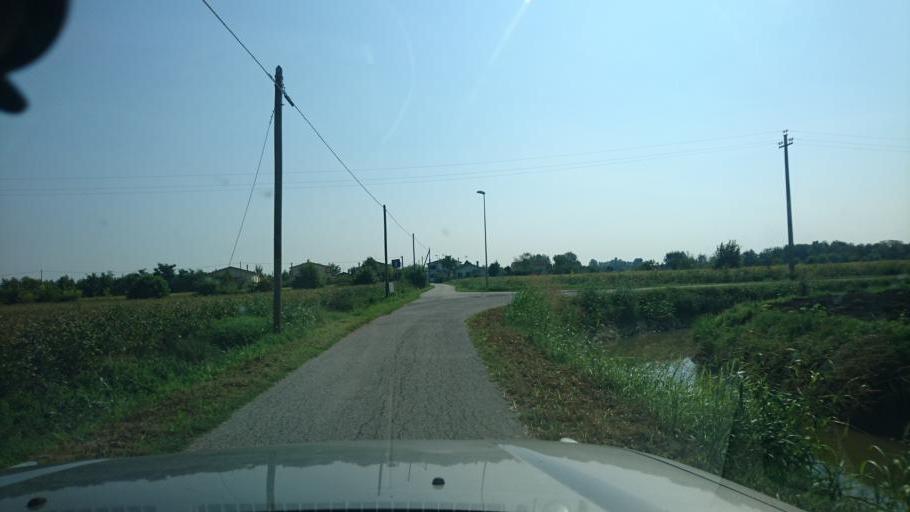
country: IT
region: Veneto
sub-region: Provincia di Padova
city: Bovolenta
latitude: 45.2845
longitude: 11.9180
